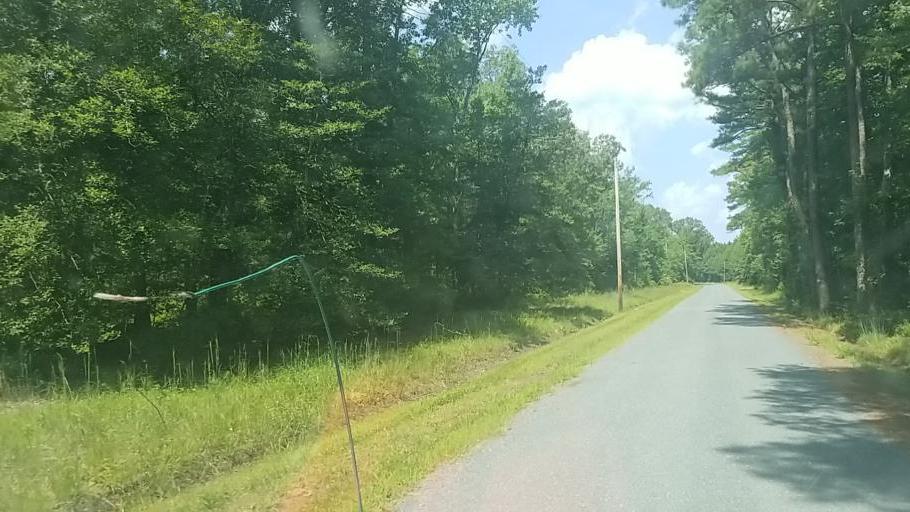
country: US
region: Maryland
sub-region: Worcester County
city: Snow Hill
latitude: 38.2459
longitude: -75.4140
